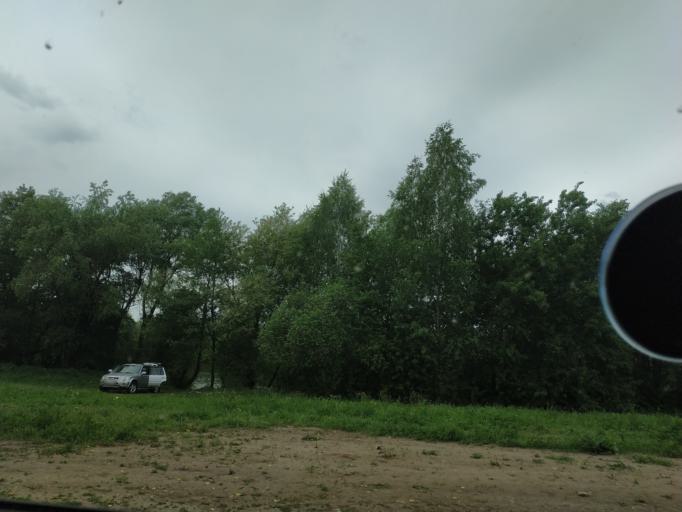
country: RU
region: Moskovskaya
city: Ostrovtsy
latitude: 55.5585
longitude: 38.0281
